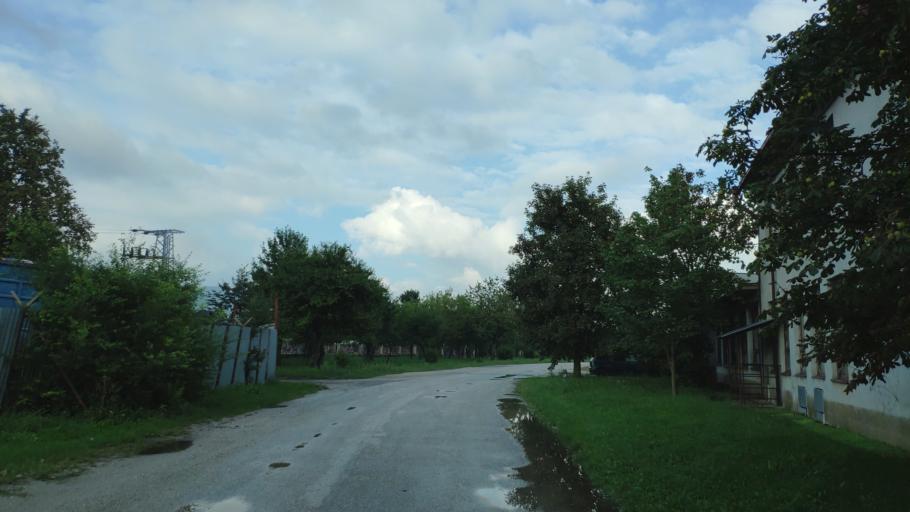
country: SK
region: Kosicky
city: Medzev
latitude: 48.5980
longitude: 20.8882
